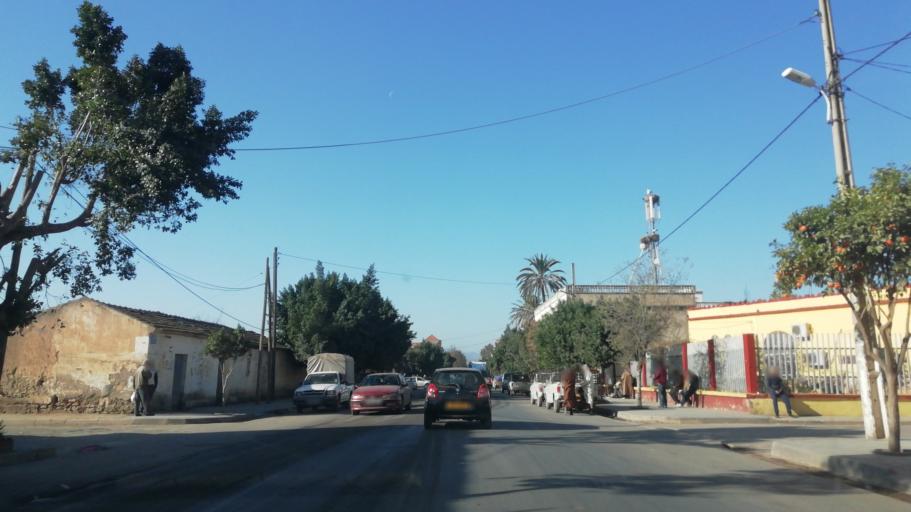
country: DZ
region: Mascara
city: Mascara
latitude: 35.6204
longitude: 0.1132
